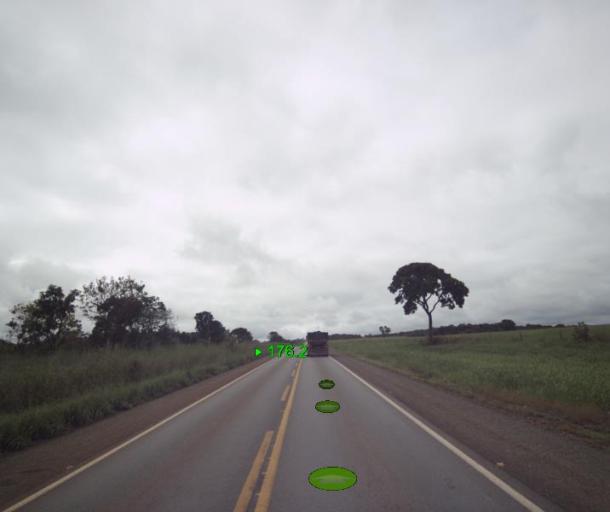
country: BR
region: Goias
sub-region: Uruacu
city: Uruacu
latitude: -14.6677
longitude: -49.1471
